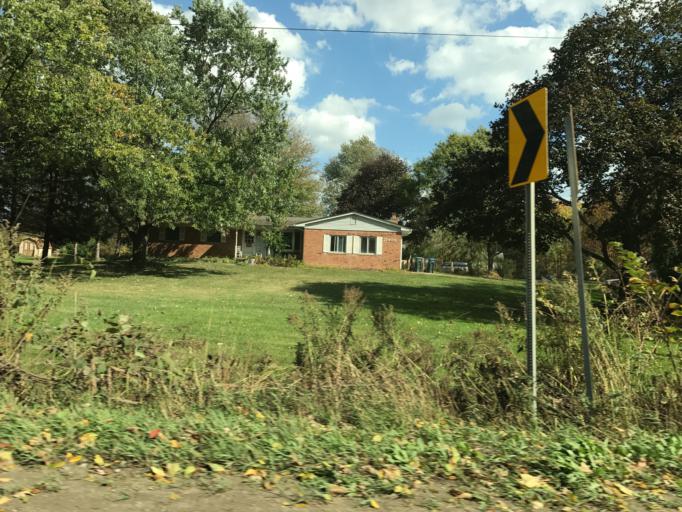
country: US
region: Michigan
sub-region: Oakland County
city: South Lyon
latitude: 42.4875
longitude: -83.6130
